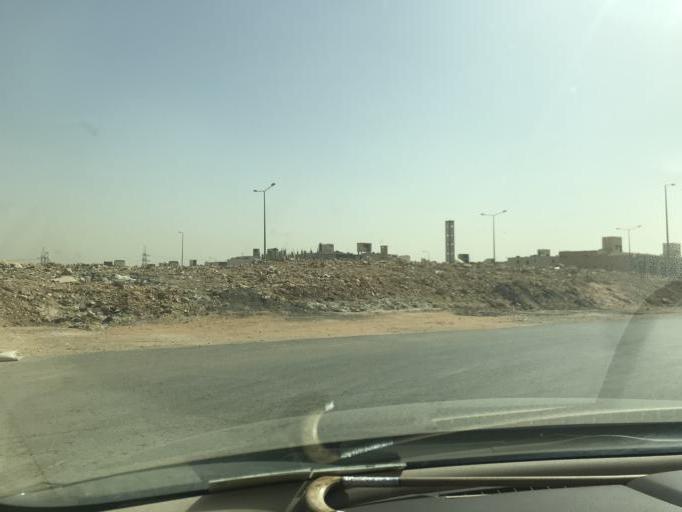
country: SA
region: Ar Riyad
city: Riyadh
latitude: 24.8259
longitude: 46.7312
